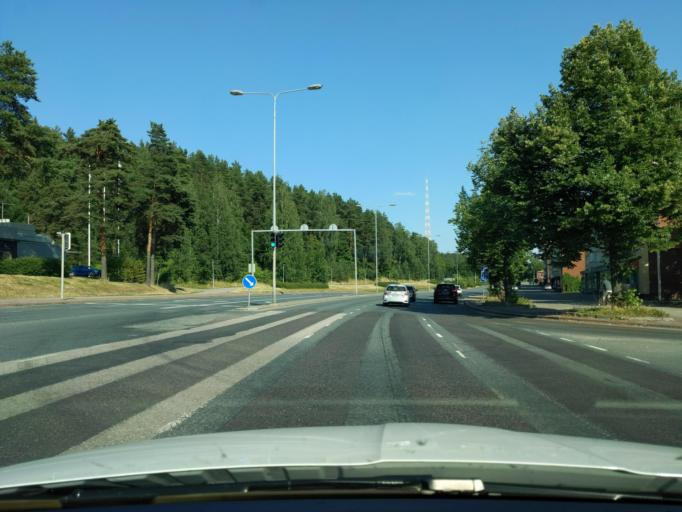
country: FI
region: Paijanne Tavastia
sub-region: Lahti
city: Lahti
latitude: 60.9812
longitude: 25.6273
